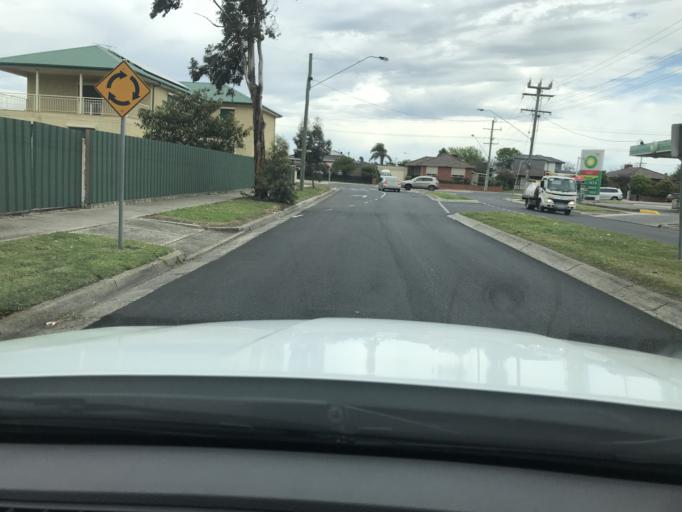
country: AU
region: Victoria
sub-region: Hume
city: Craigieburn
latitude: -37.5926
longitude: 144.9382
